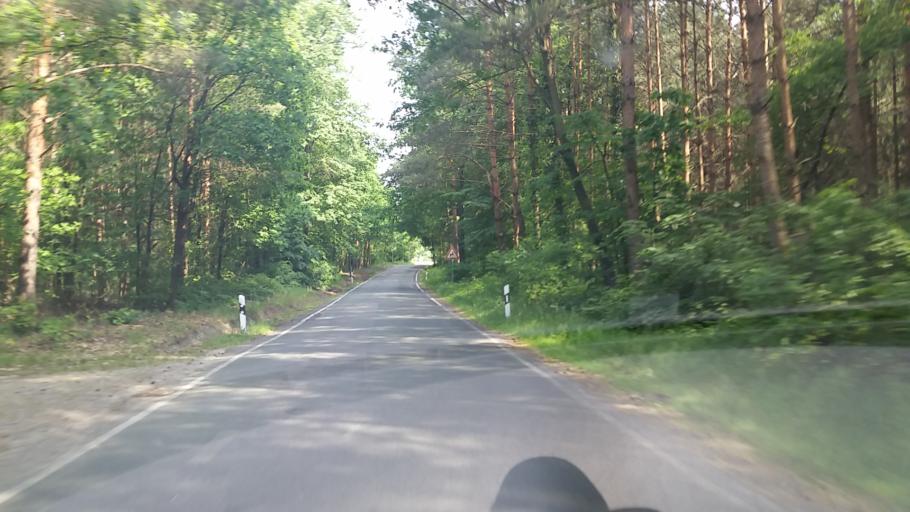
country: DE
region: Saxony
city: Schwepnitz
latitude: 51.3659
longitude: 13.9702
